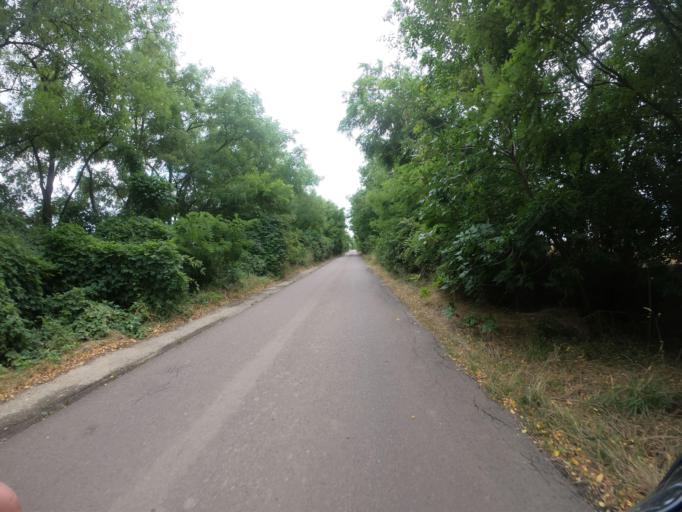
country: HU
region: Borsod-Abauj-Zemplen
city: Szentistvan
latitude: 47.7353
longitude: 20.6829
